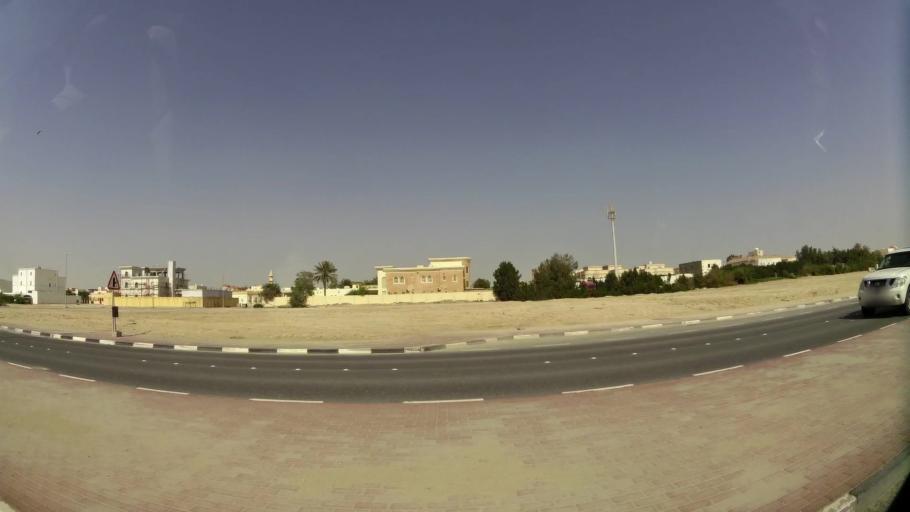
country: QA
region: Baladiyat Umm Salal
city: Umm Salal Muhammad
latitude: 25.3721
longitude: 51.4336
